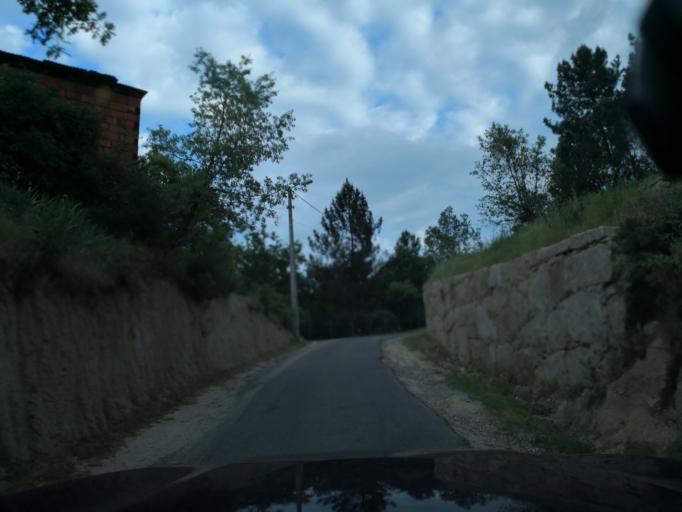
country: PT
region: Vila Real
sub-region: Vila Real
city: Vila Real
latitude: 41.3094
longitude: -7.7736
